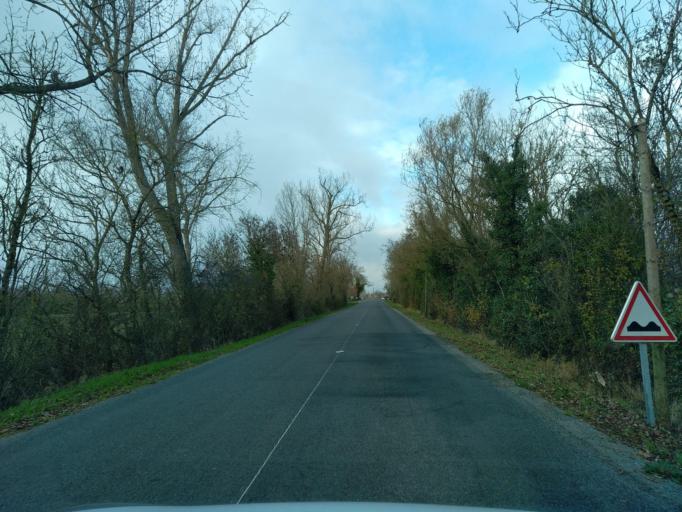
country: FR
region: Pays de la Loire
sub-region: Departement de la Vendee
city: Vix
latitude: 46.3431
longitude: -0.8285
